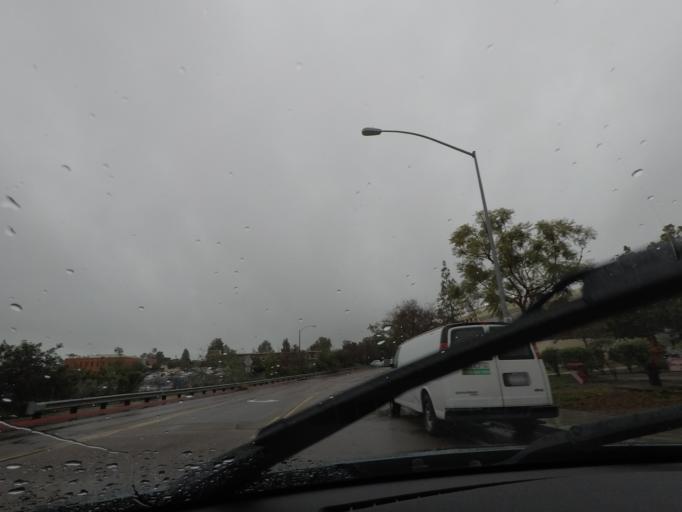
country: US
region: California
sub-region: San Diego County
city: San Diego
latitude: 32.7963
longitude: -117.1513
